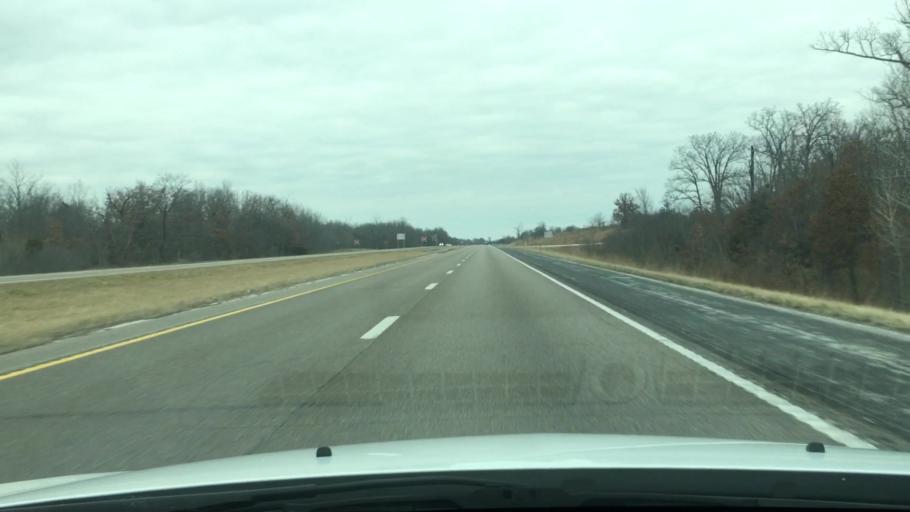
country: US
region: Missouri
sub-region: Callaway County
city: Fulton
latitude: 38.9869
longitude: -91.8938
